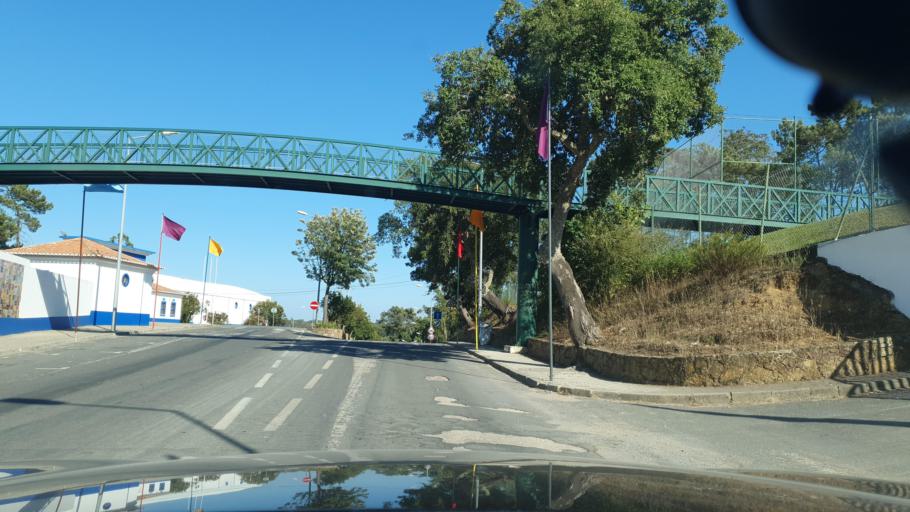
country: PT
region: Beja
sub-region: Odemira
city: Sao Teotonio
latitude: 37.5092
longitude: -8.7107
